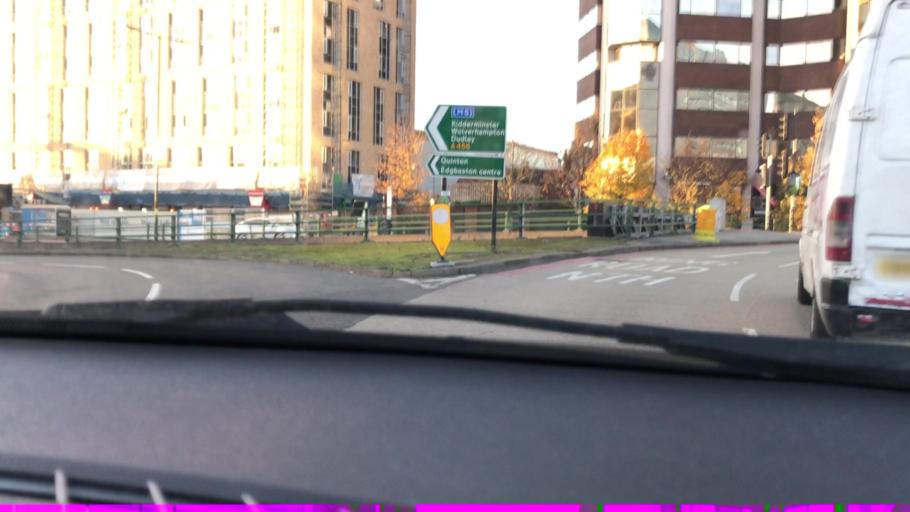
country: GB
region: England
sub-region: City and Borough of Birmingham
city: Birmingham
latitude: 52.4725
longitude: -1.9188
